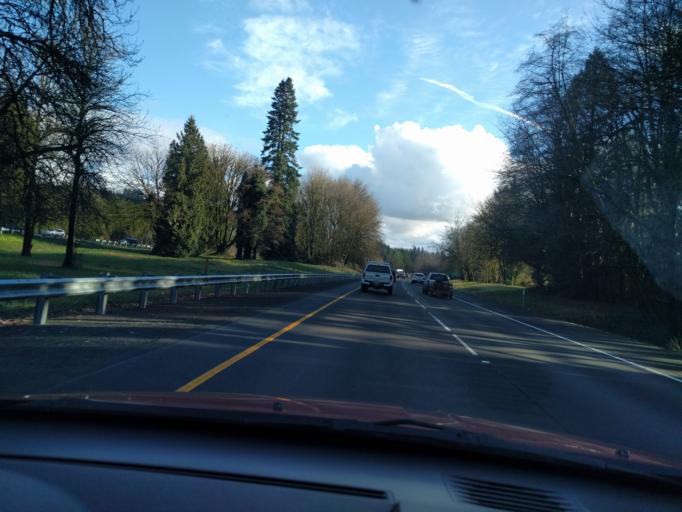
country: US
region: Oregon
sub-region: Clackamas County
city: Stafford
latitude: 45.3636
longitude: -122.6737
